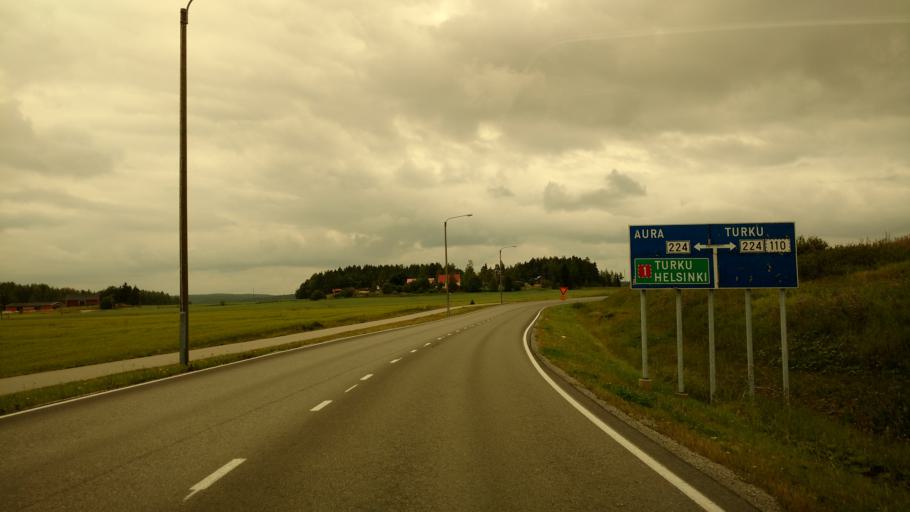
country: FI
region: Varsinais-Suomi
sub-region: Salo
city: Halikko
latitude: 60.4136
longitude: 23.0523
